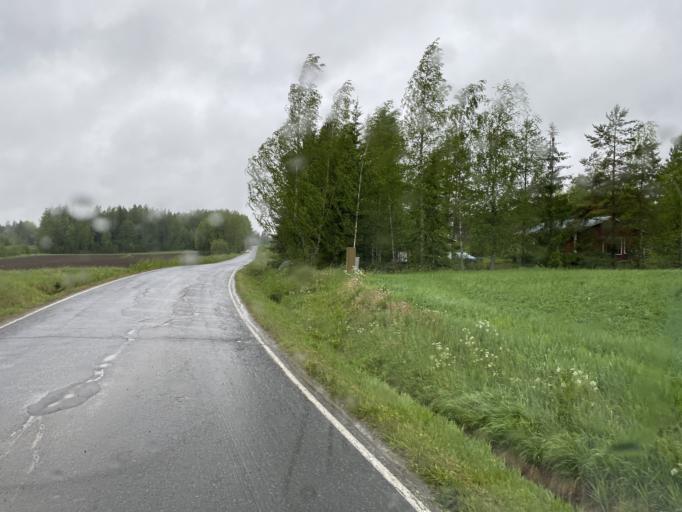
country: FI
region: Pirkanmaa
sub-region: Etelae-Pirkanmaa
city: Urjala
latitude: 60.9753
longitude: 23.5444
